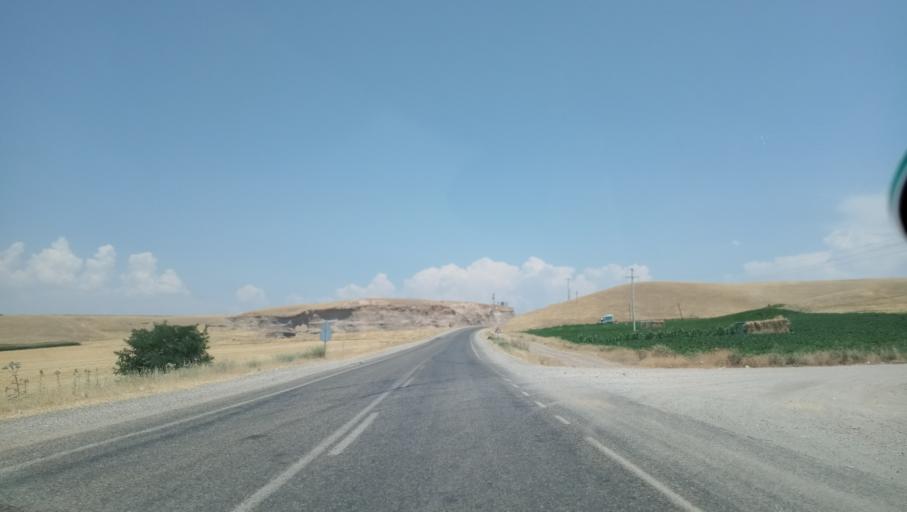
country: TR
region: Diyarbakir
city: Aralik
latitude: 37.8086
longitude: 40.7176
